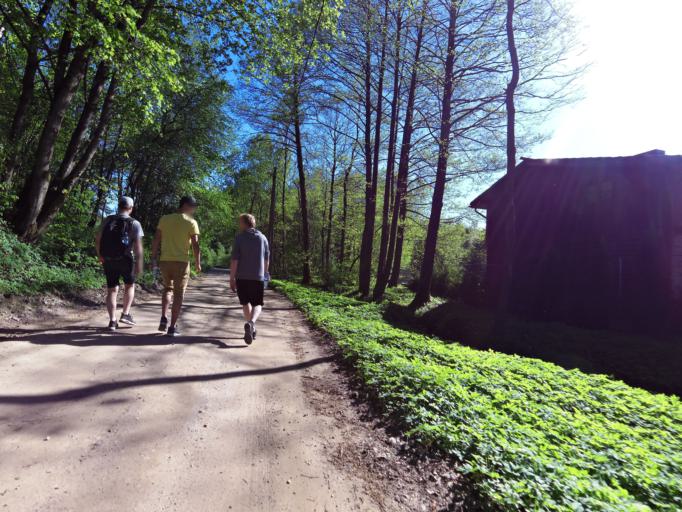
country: LT
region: Vilnius County
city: Pilaite
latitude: 54.6877
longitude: 25.1556
